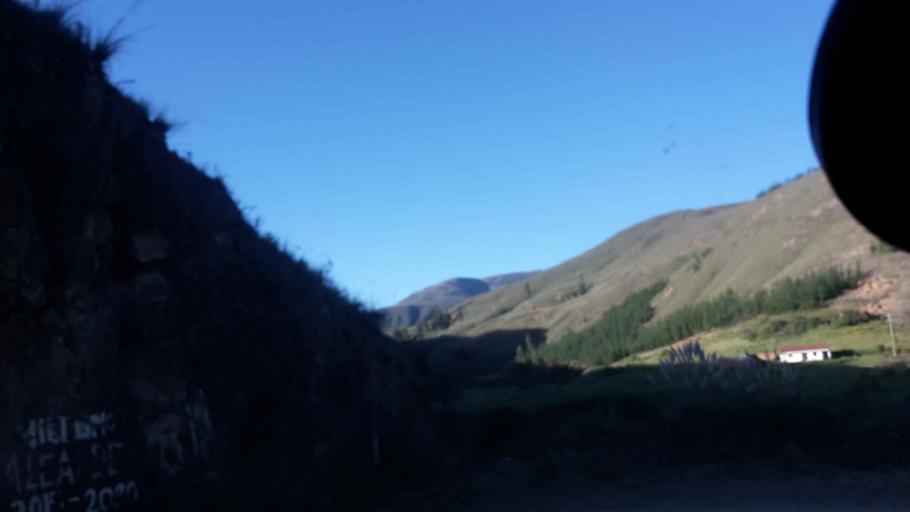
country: BO
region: Cochabamba
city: Arani
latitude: -17.7954
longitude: -65.5987
